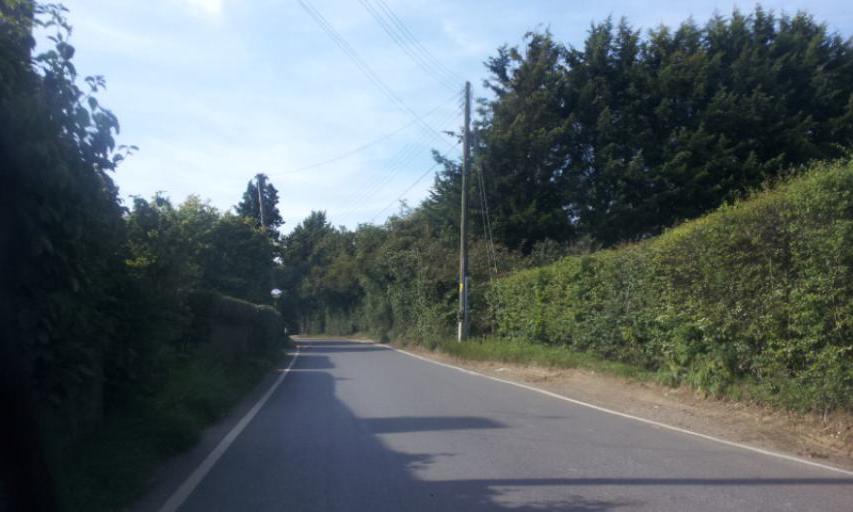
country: GB
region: England
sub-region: Kent
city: Newington
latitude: 51.3271
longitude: 0.6856
